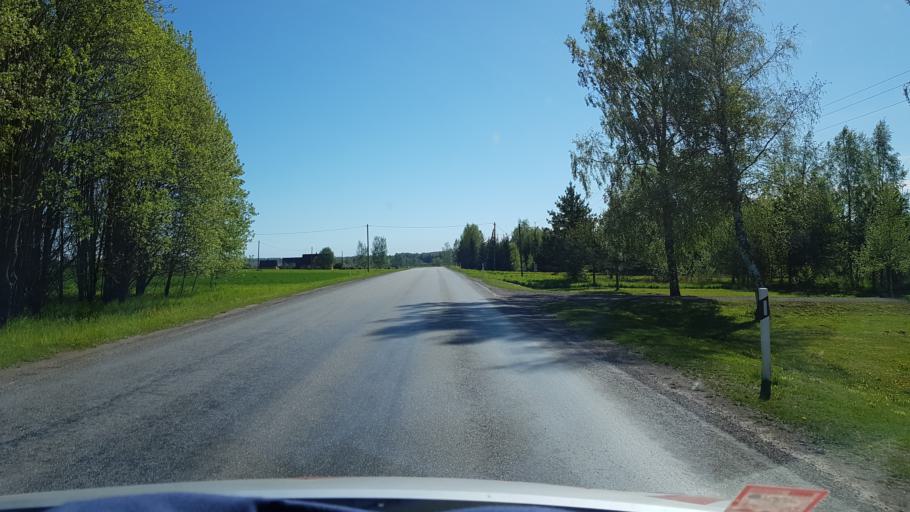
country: EE
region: Polvamaa
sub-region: Polva linn
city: Polva
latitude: 58.2827
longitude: 27.0089
